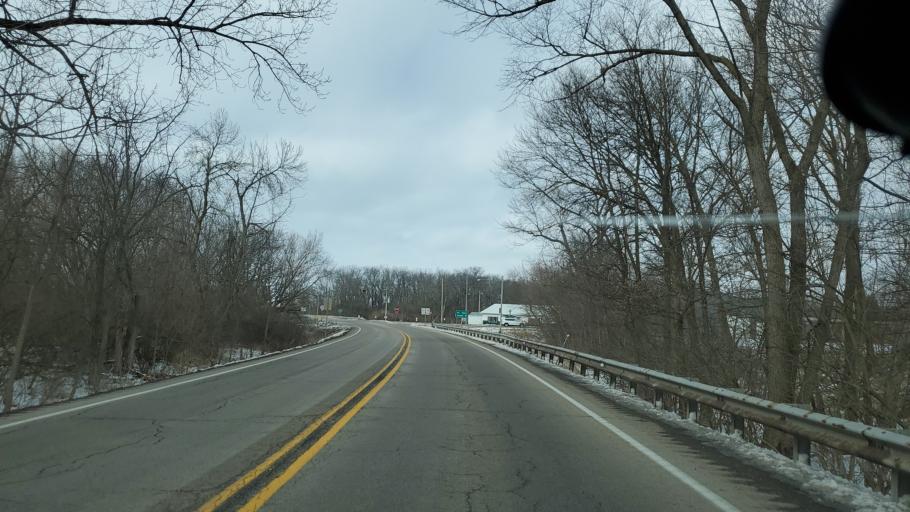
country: US
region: Illinois
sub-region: Marshall County
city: Toluca
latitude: 41.1172
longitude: -89.2014
